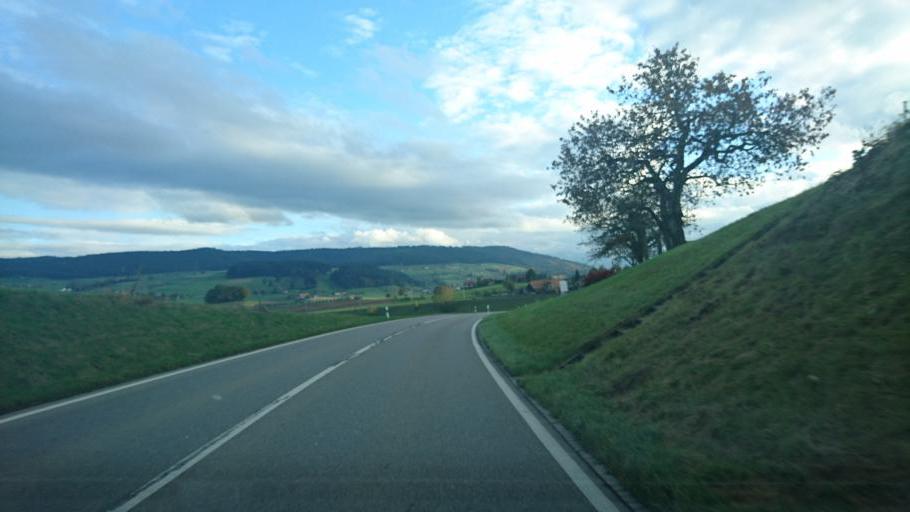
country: CH
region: Bern
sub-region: Bern-Mittelland District
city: Konolfingen
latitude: 46.8978
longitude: 7.6339
